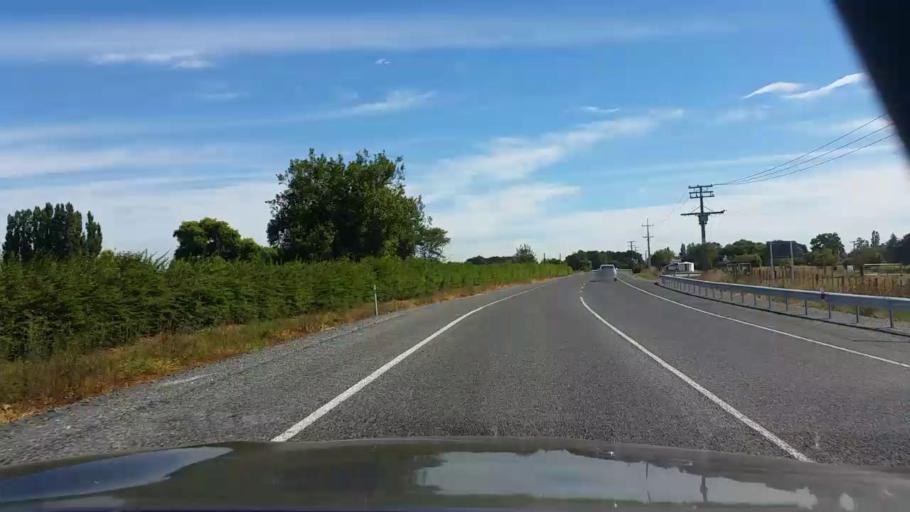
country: NZ
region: Waikato
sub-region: Hamilton City
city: Hamilton
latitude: -37.6681
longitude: 175.3012
